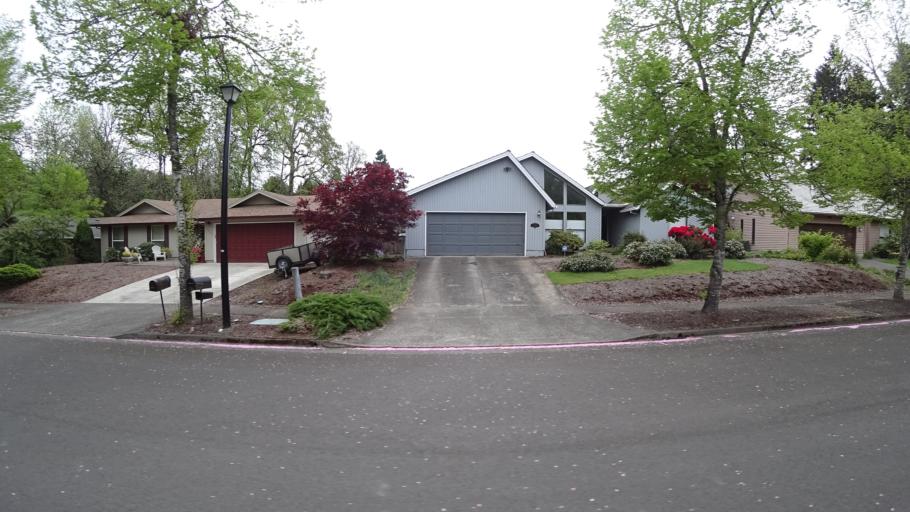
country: US
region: Oregon
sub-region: Washington County
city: Beaverton
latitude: 45.4626
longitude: -122.8274
